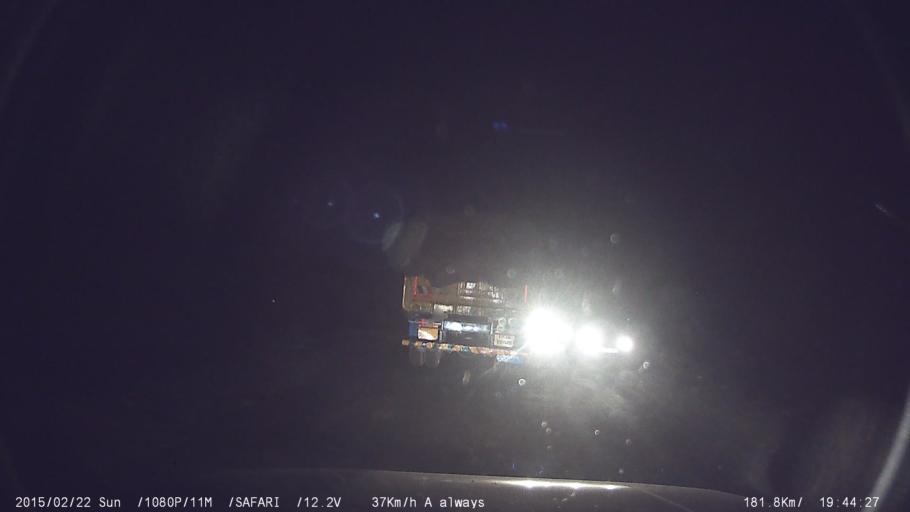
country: IN
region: Tamil Nadu
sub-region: Theni
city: Devadanappatti
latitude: 10.1487
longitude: 77.6574
